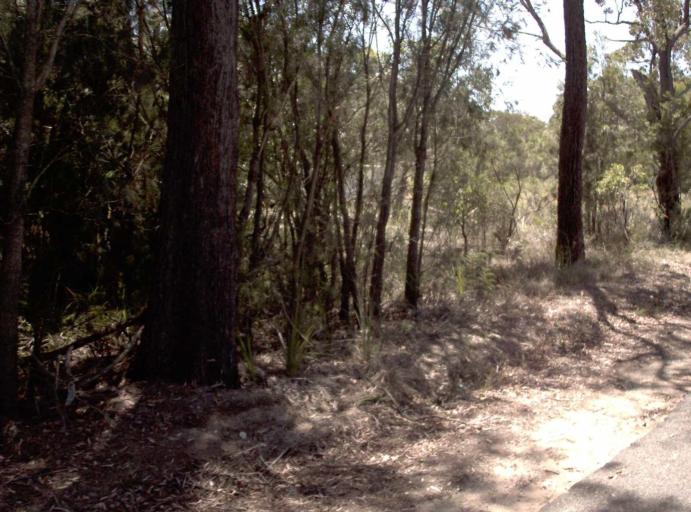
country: AU
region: Victoria
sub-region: East Gippsland
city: Lakes Entrance
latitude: -37.8297
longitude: 148.0320
